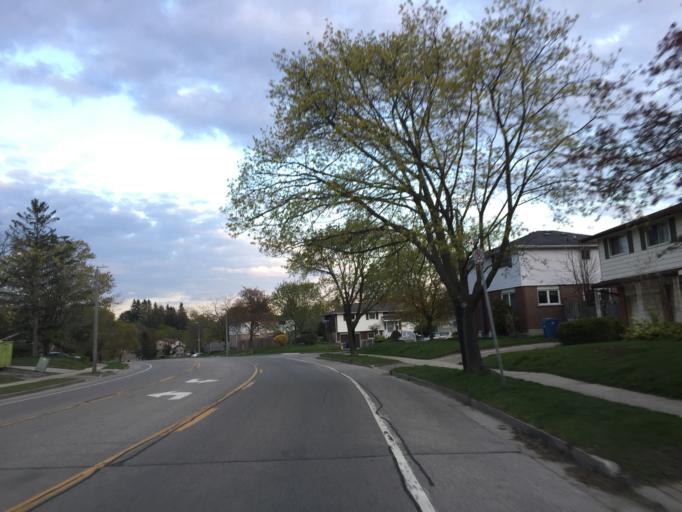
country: CA
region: Ontario
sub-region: Wellington County
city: Guelph
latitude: 43.5113
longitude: -80.2524
